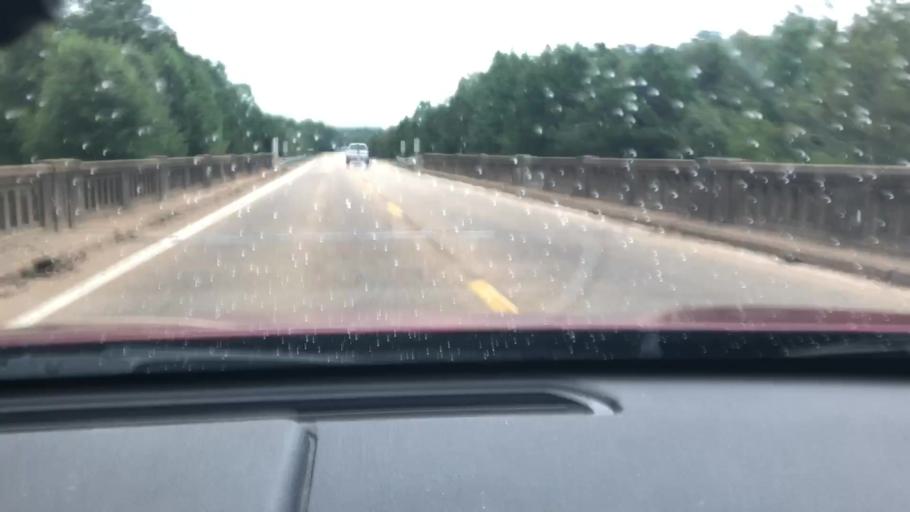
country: US
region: Arkansas
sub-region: Lafayette County
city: Stamps
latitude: 33.3670
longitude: -93.5225
